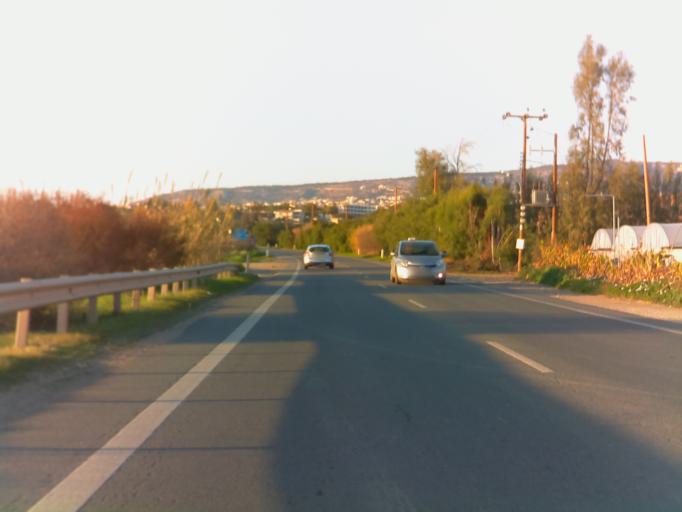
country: CY
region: Pafos
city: Kissonerga
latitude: 34.8473
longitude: 32.3857
